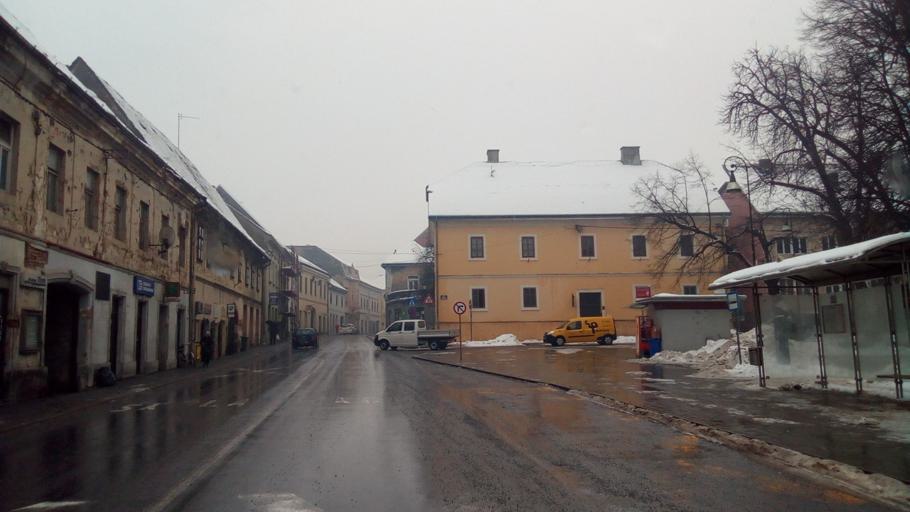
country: HR
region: Sisacko-Moslavacka
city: Petrinja
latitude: 45.4418
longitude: 16.2774
